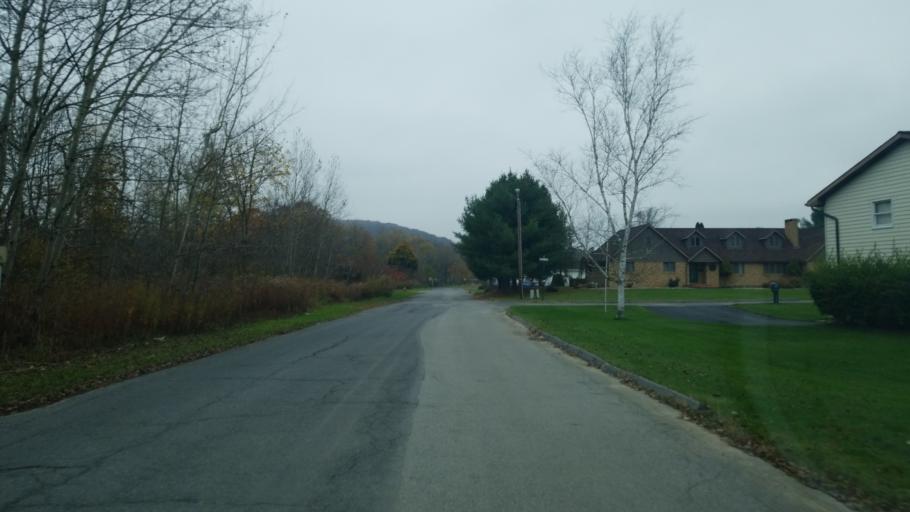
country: US
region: Pennsylvania
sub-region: Clearfield County
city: Clearfield
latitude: 41.0069
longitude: -78.4411
